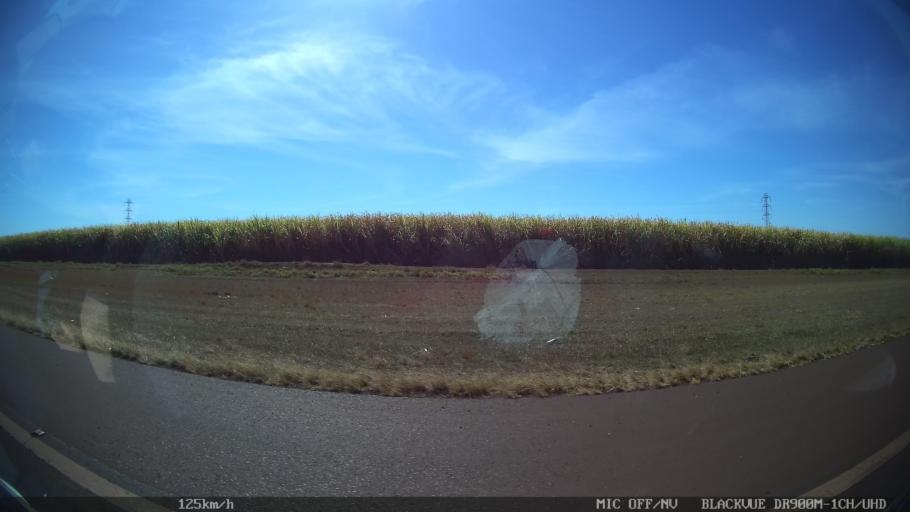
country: BR
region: Sao Paulo
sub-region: Guaira
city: Guaira
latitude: -20.4490
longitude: -48.1903
